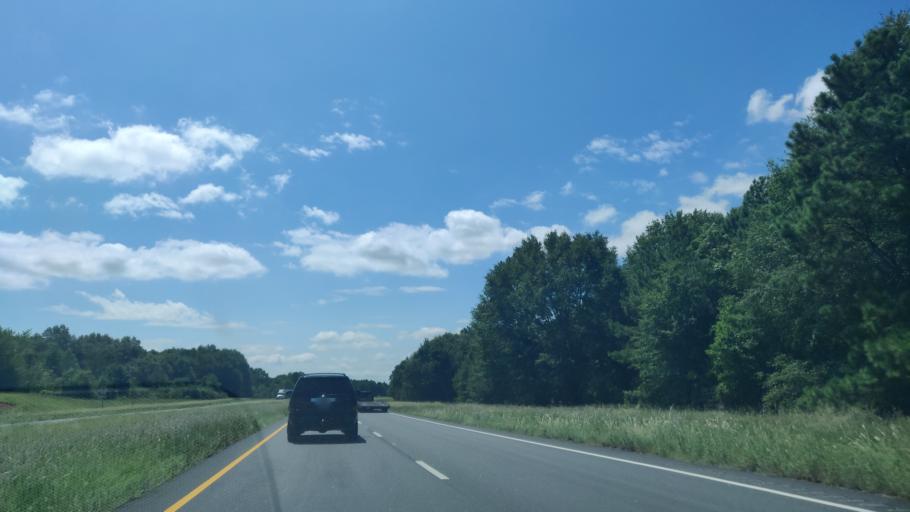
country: US
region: Georgia
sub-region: Stewart County
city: Richland
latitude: 32.1339
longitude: -84.6855
